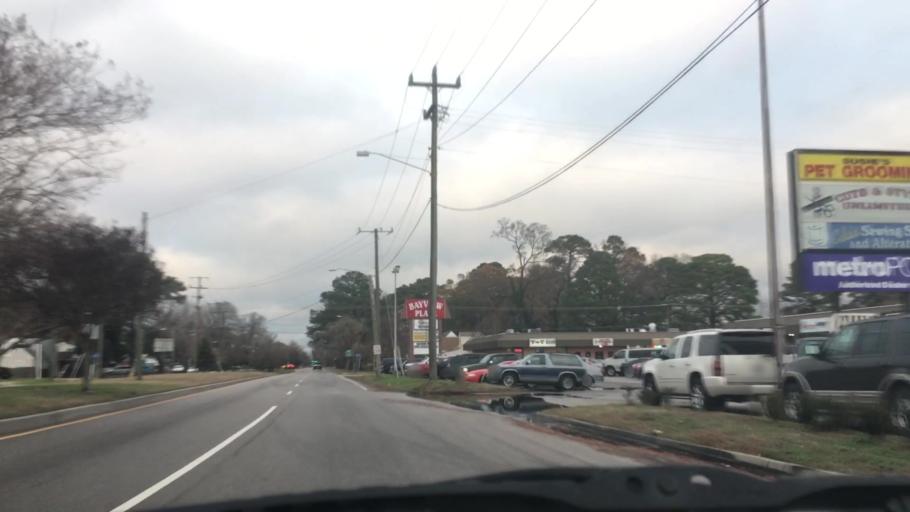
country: US
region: Virginia
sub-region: City of Norfolk
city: Norfolk
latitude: 36.9155
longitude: -76.2414
